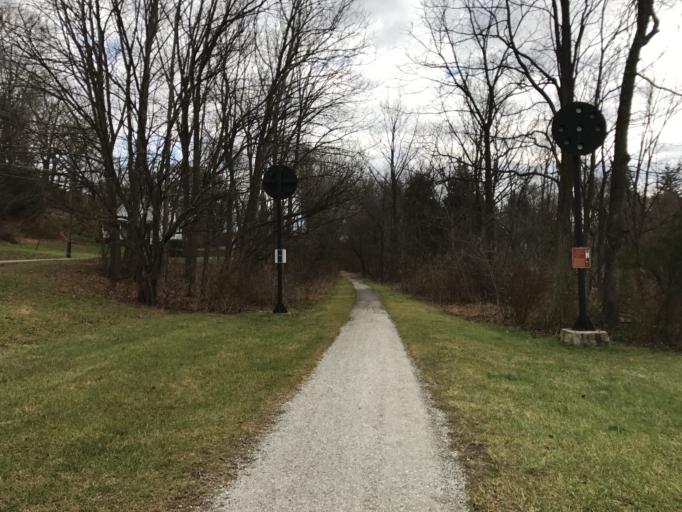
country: US
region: Maryland
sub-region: Baltimore County
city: Hunt Valley
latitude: 39.6216
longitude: -76.6289
